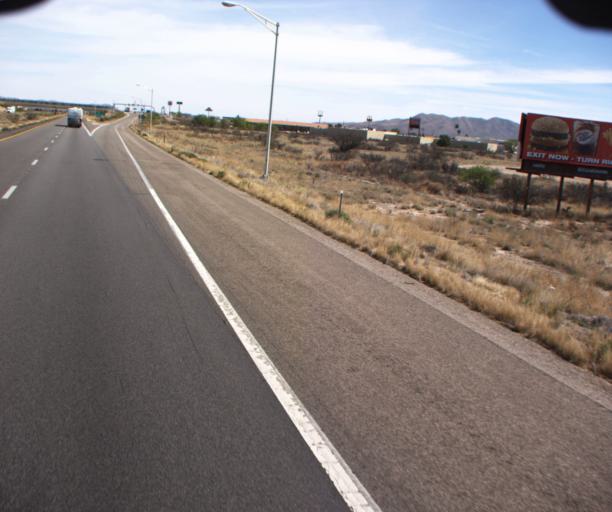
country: US
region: Arizona
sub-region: Cochise County
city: Willcox
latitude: 32.2617
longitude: -109.8473
